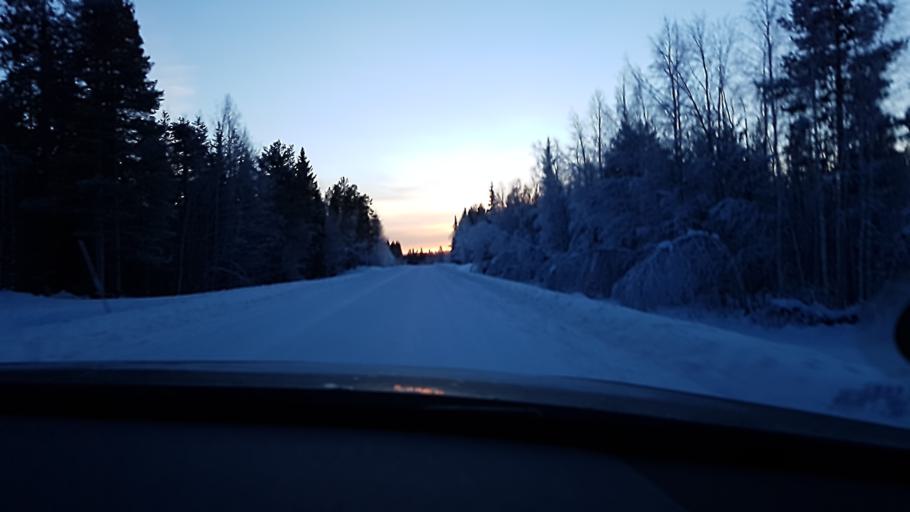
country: SE
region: Vaesterbotten
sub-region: Storumans Kommun
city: Storuman
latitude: 65.1568
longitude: 17.2624
